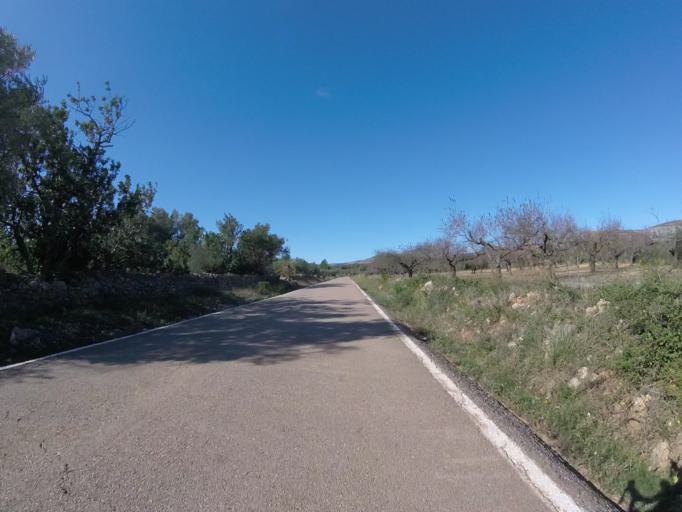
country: ES
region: Valencia
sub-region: Provincia de Castello
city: Chert/Xert
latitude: 40.4506
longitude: 0.1178
